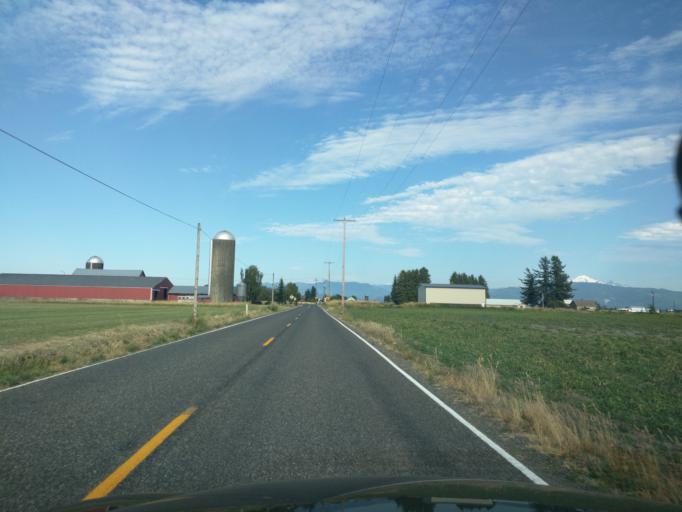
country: US
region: Washington
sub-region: Whatcom County
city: Lynden
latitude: 48.9933
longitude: -122.4887
